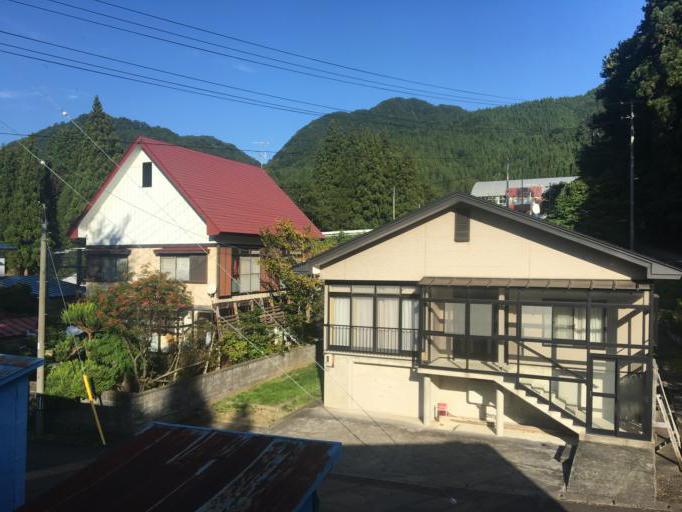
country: JP
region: Akita
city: Takanosu
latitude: 39.9936
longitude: 140.4014
